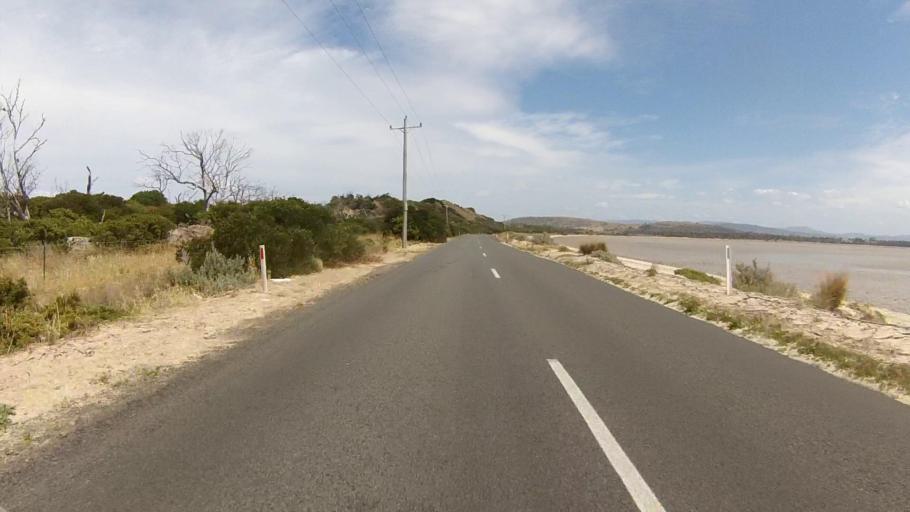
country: AU
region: Tasmania
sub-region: Clarence
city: Sandford
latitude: -43.0305
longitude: 147.4617
